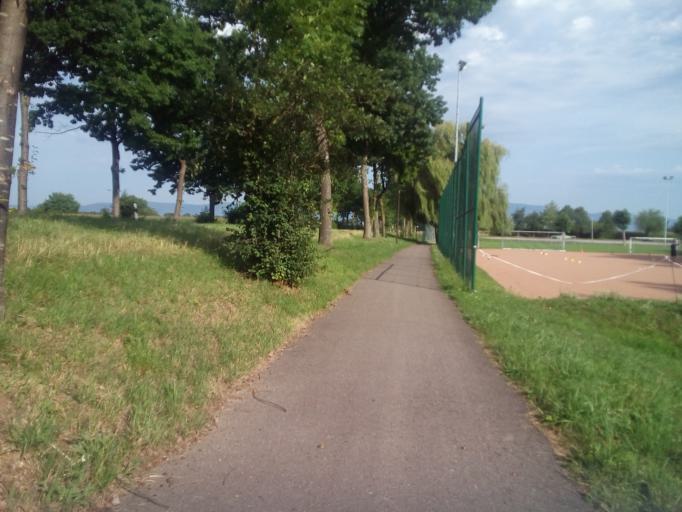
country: DE
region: Baden-Wuerttemberg
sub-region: Karlsruhe Region
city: Lichtenau
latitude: 48.7235
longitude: 8.0228
